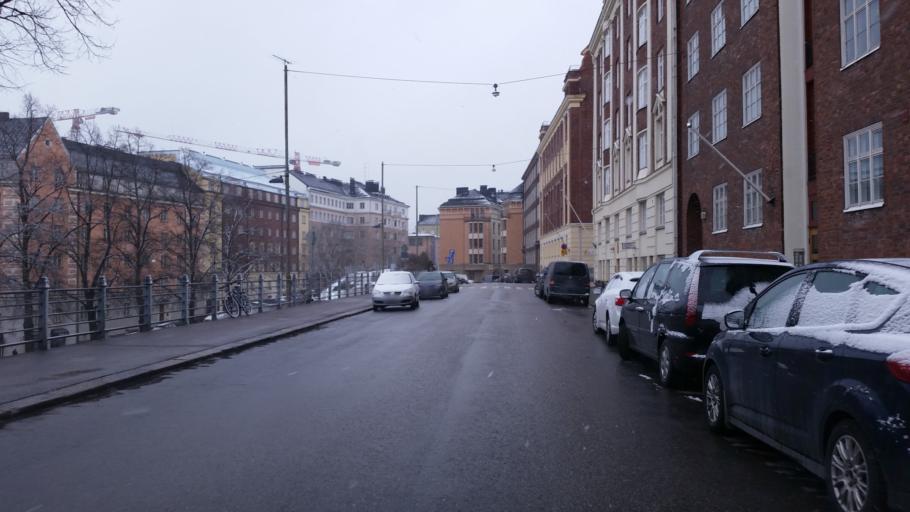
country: FI
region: Uusimaa
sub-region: Helsinki
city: Helsinki
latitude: 60.1734
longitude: 24.9278
